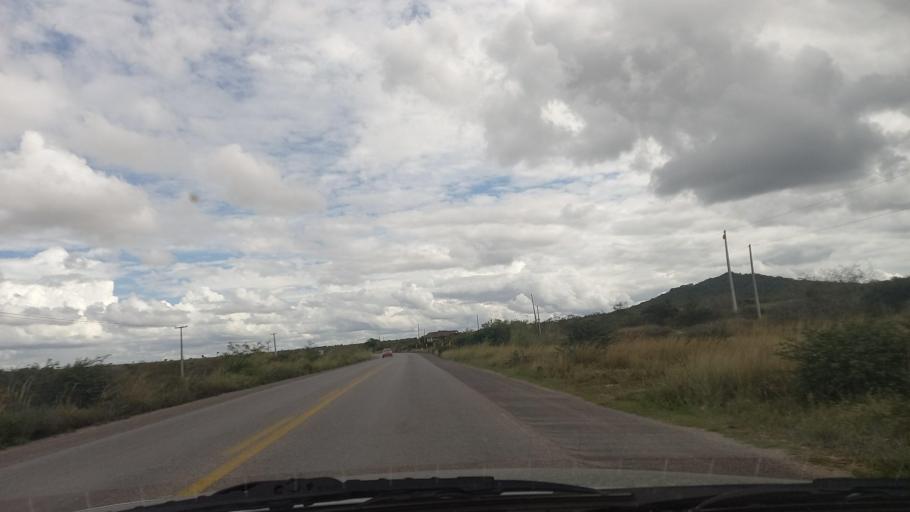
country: BR
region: Pernambuco
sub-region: Cachoeirinha
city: Cachoeirinha
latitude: -8.3493
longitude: -36.1687
